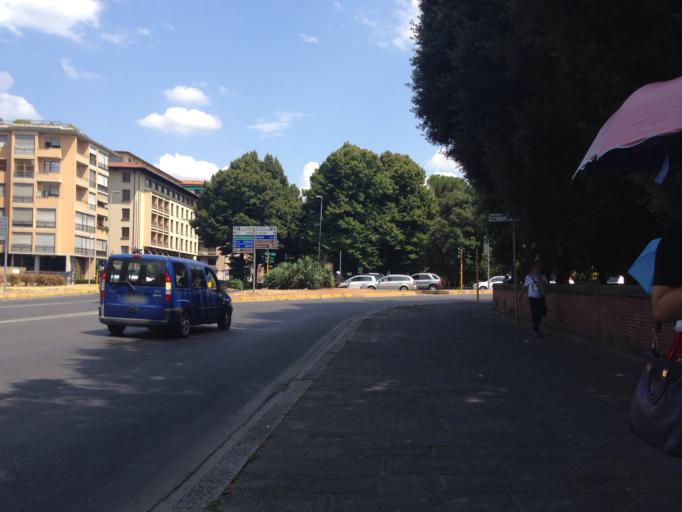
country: IT
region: Tuscany
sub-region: Province of Florence
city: Florence
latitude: 43.7660
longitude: 11.2706
